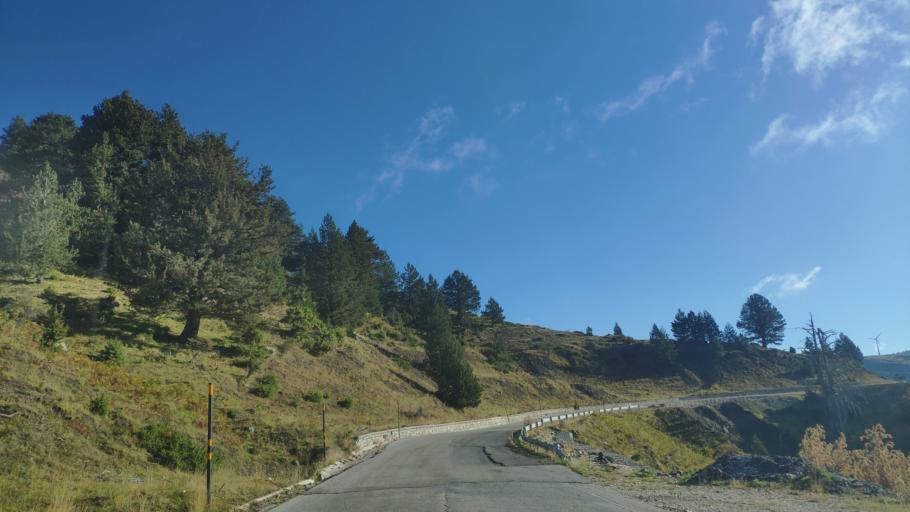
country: GR
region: Epirus
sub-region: Nomos Ioanninon
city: Metsovo
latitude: 39.7975
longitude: 21.1696
